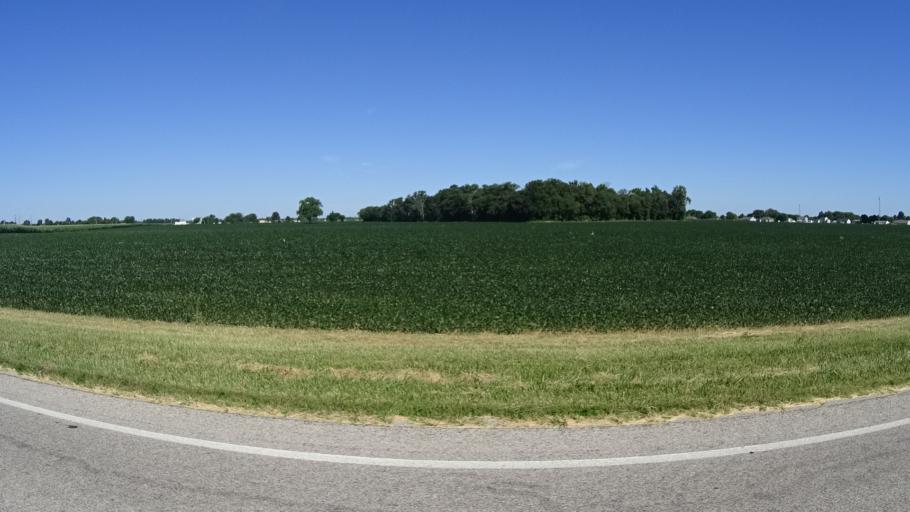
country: US
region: Ohio
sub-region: Erie County
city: Sandusky
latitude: 41.3903
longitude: -82.7209
